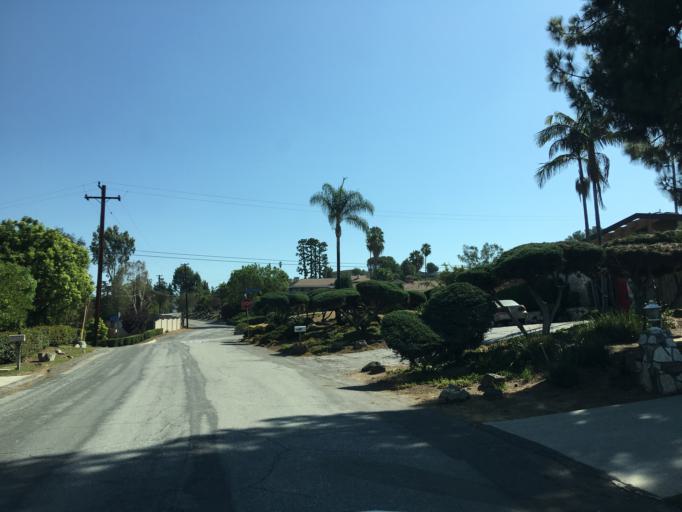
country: US
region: California
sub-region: Los Angeles County
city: Charter Oak
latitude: 34.0788
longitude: -117.8577
